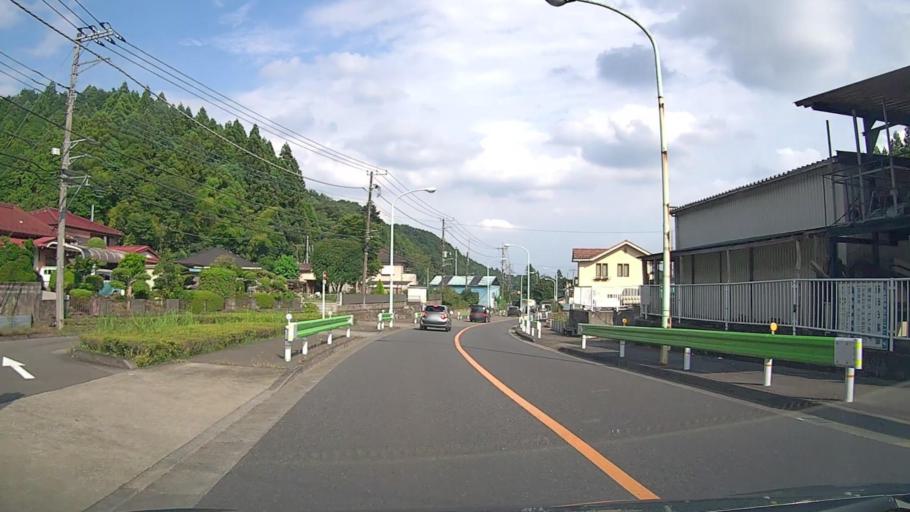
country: JP
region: Tokyo
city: Itsukaichi
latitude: 35.7122
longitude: 139.2336
